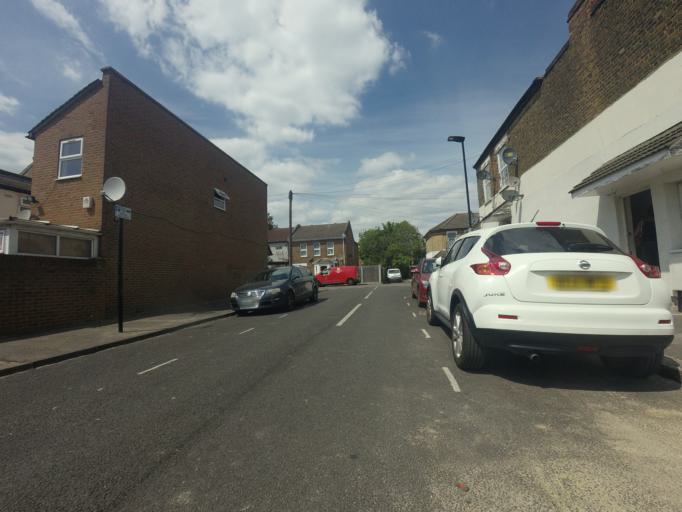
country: GB
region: England
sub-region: Greater London
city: East Ham
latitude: 51.5539
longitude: 0.0188
